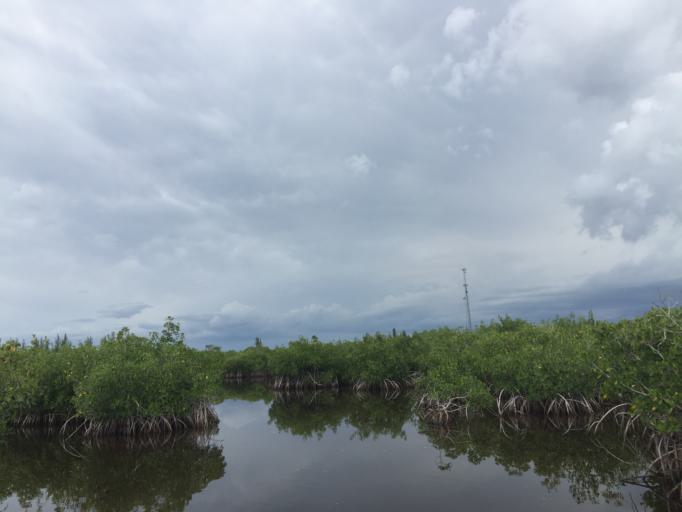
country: US
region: Florida
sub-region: Collier County
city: Marco
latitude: 25.9072
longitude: -81.3714
